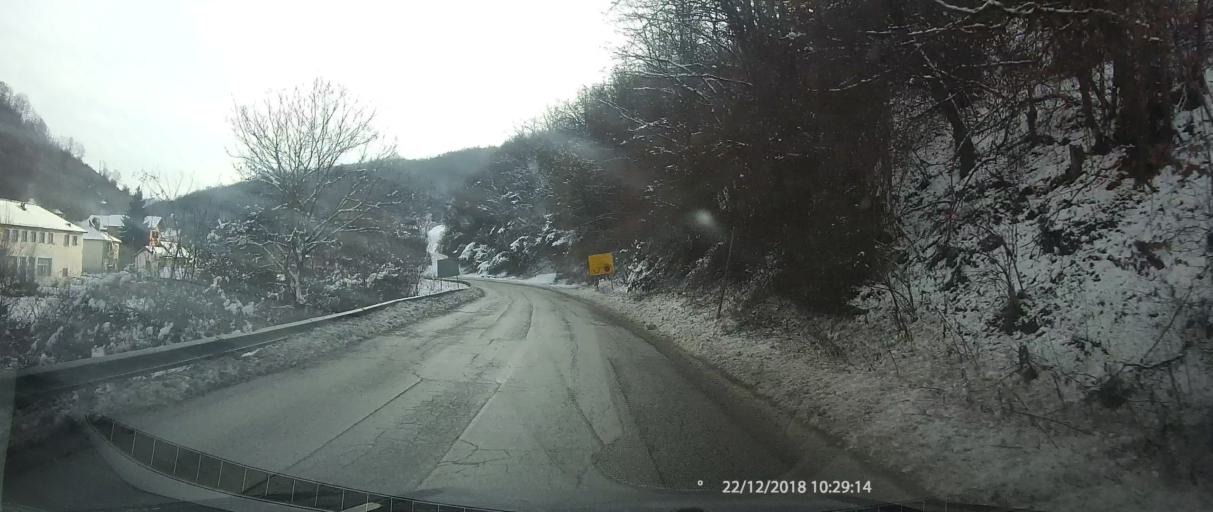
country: MK
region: Kriva Palanka
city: Kriva Palanka
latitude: 42.2237
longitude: 22.3936
